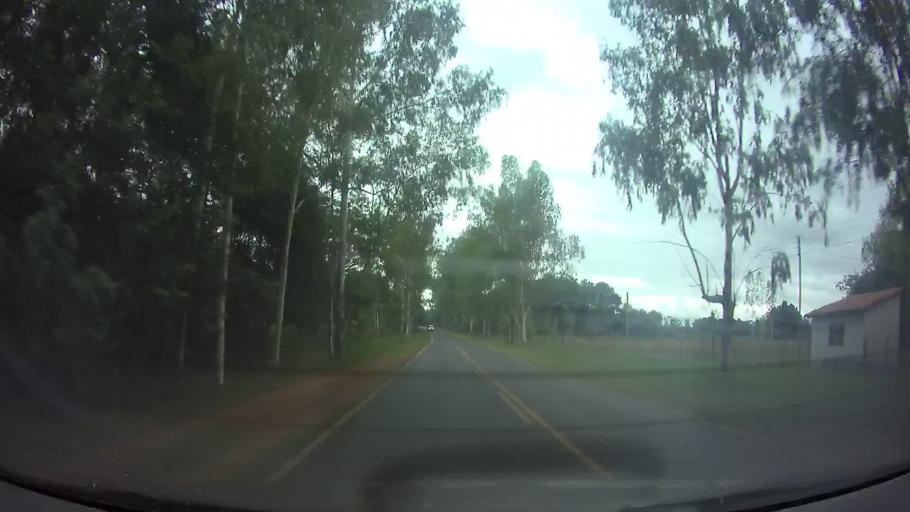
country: PY
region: Central
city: Nueva Italia
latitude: -25.5505
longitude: -57.5013
